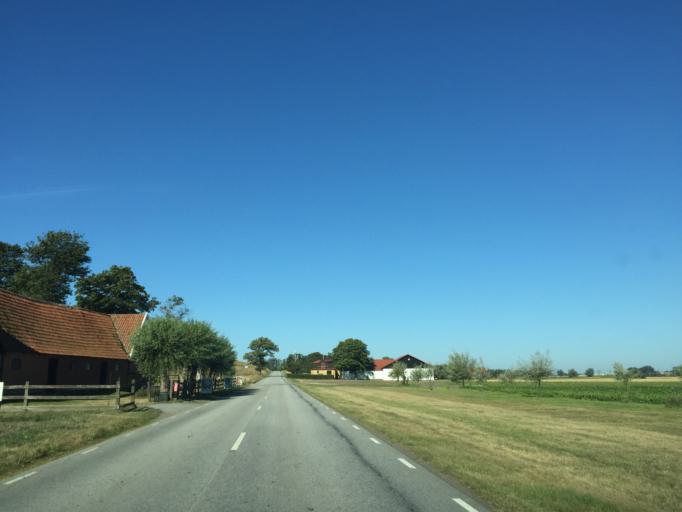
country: SE
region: Skane
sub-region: Ystads Kommun
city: Kopingebro
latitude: 55.3906
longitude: 14.0848
